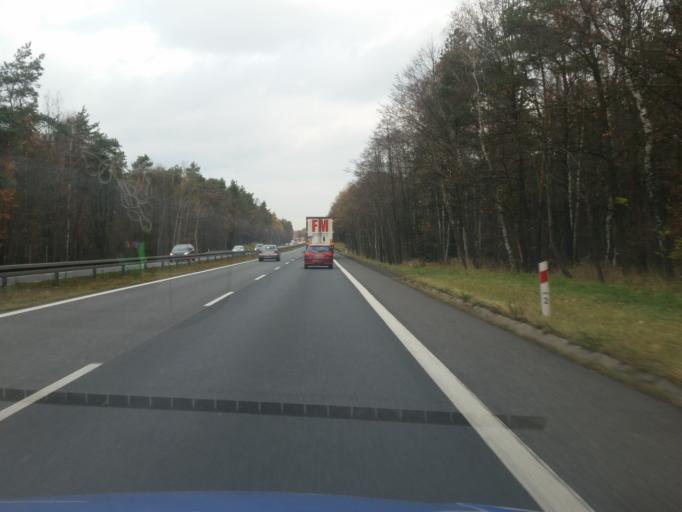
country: PL
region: Silesian Voivodeship
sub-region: Powiat czestochowski
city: Kamienica Polska
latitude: 50.6530
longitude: 19.1324
